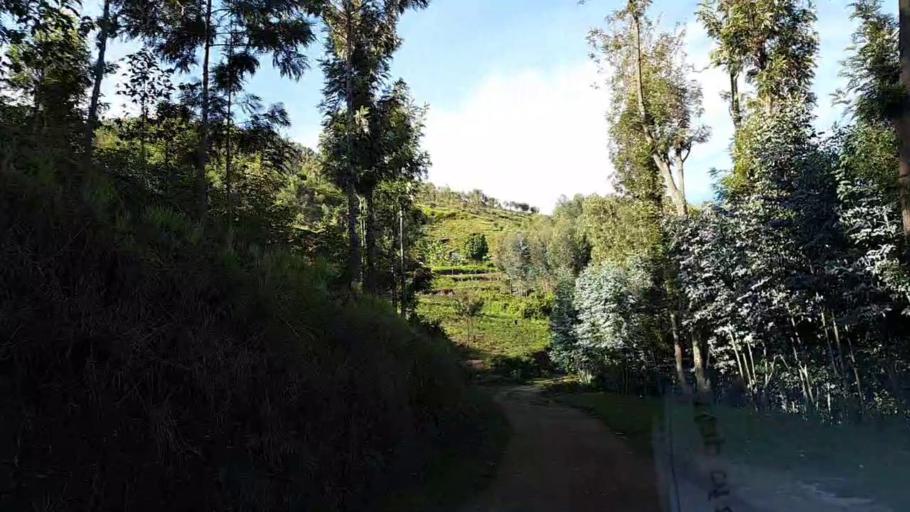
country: RW
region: Southern Province
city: Nzega
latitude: -2.4154
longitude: 29.5152
